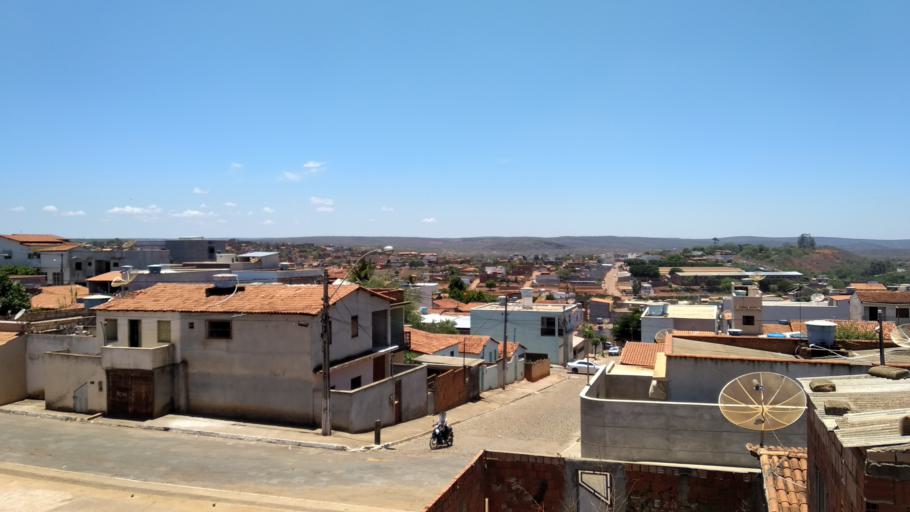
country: BR
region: Bahia
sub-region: Caetite
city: Caetite
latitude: -14.0621
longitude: -42.4841
